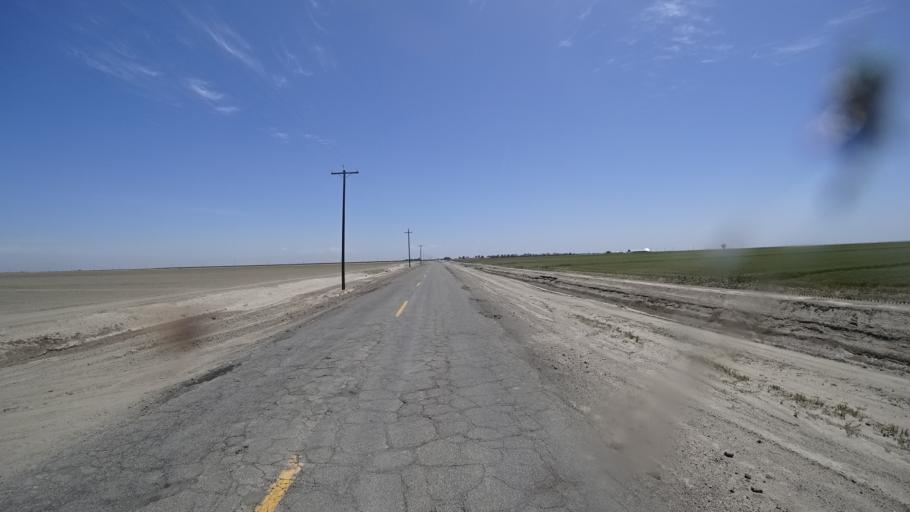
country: US
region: California
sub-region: Kings County
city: Corcoran
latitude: 36.1162
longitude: -119.6558
